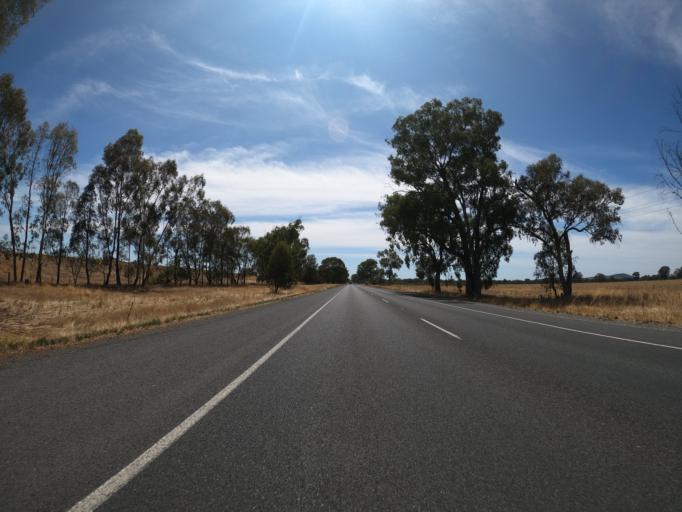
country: AU
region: Victoria
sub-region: Benalla
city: Benalla
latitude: -36.5284
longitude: 146.0452
